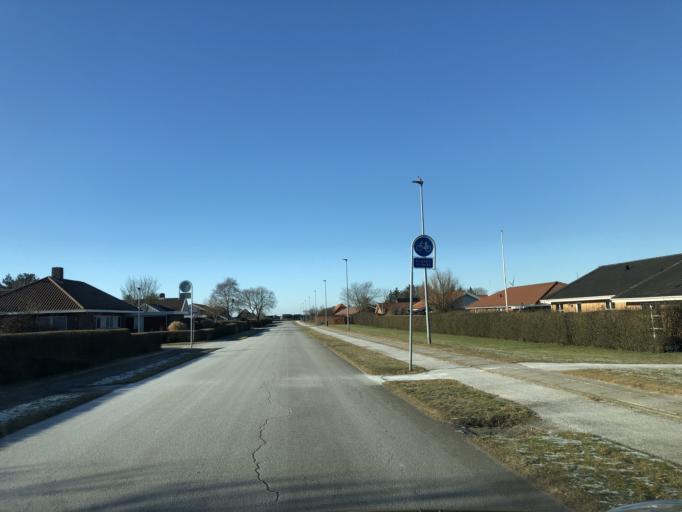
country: DK
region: Central Jutland
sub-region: Ringkobing-Skjern Kommune
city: Ringkobing
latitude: 56.1004
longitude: 8.2593
